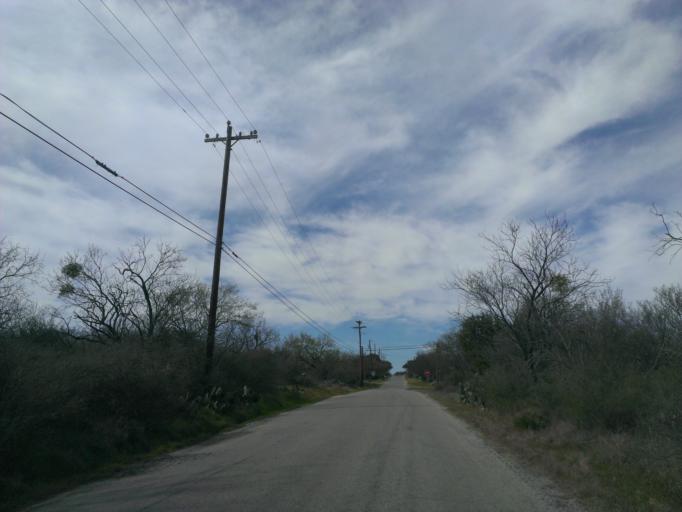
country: US
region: Texas
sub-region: Burnet County
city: Granite Shoals
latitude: 30.5789
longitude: -98.3925
